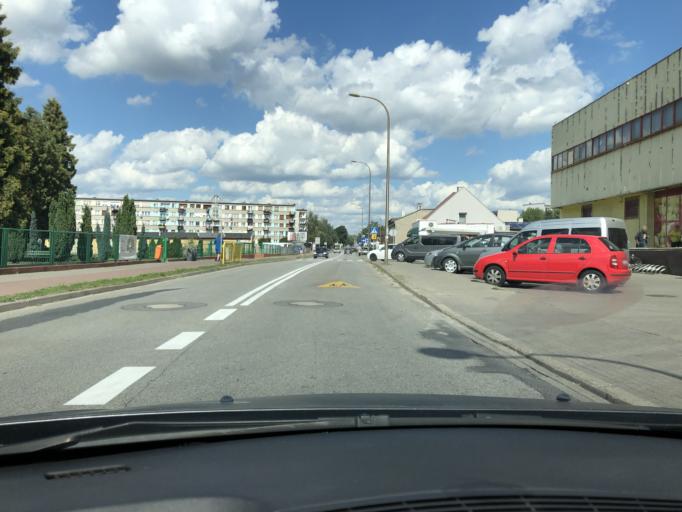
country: PL
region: Lodz Voivodeship
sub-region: Powiat wieruszowski
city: Wieruszow
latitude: 51.2953
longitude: 18.1606
